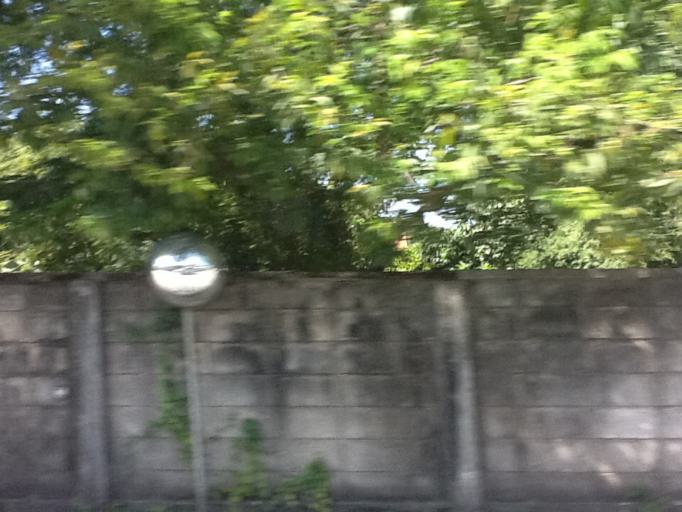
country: TH
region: Phuket
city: Thalang
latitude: 8.0882
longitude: 98.3422
